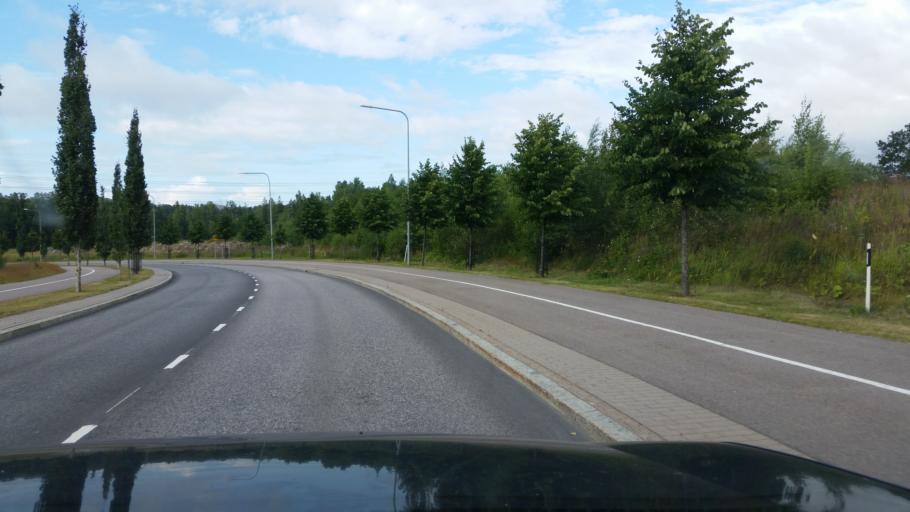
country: FI
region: Uusimaa
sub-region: Helsinki
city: Vantaa
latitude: 60.2232
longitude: 25.1619
